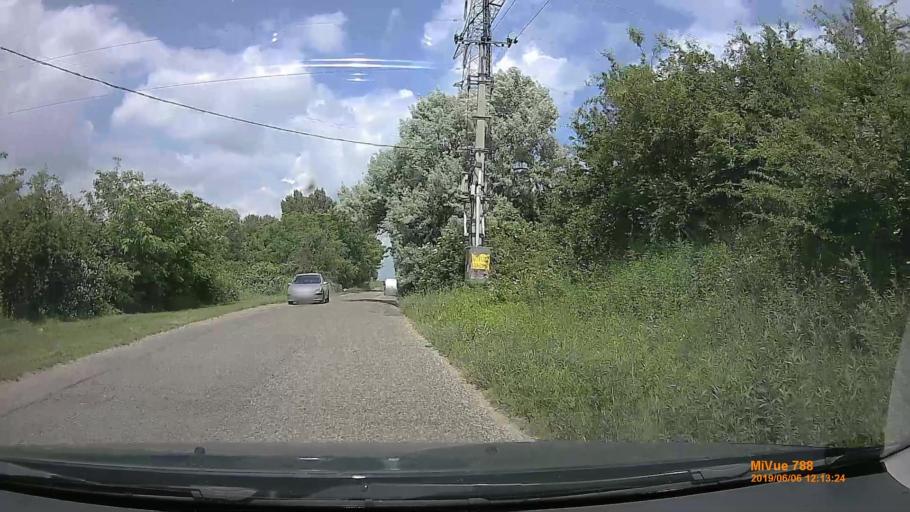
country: HU
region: Pest
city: Mogyorod
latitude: 47.5798
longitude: 19.2605
